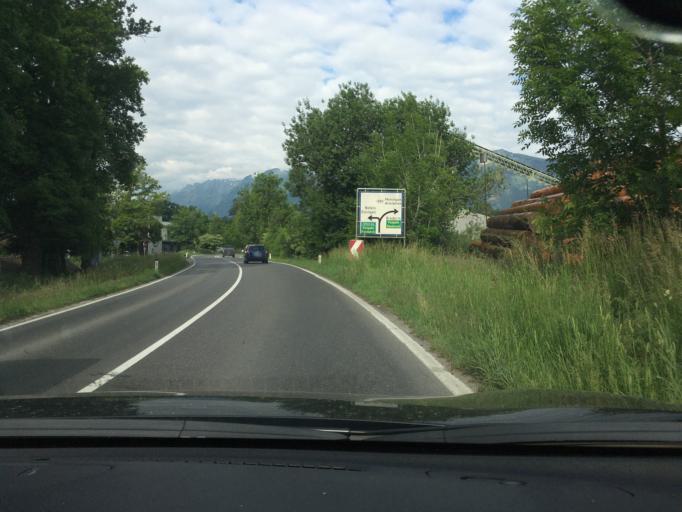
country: AT
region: Vorarlberg
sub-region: Politischer Bezirk Feldkirch
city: Nofels
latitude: 47.2762
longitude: 9.5935
